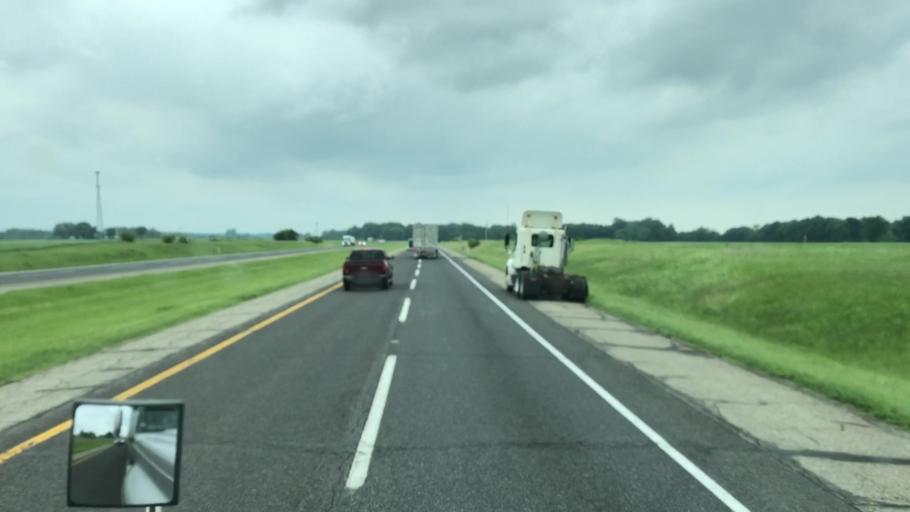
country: US
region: Michigan
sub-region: Branch County
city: Bronson
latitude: 41.7548
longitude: -85.2511
